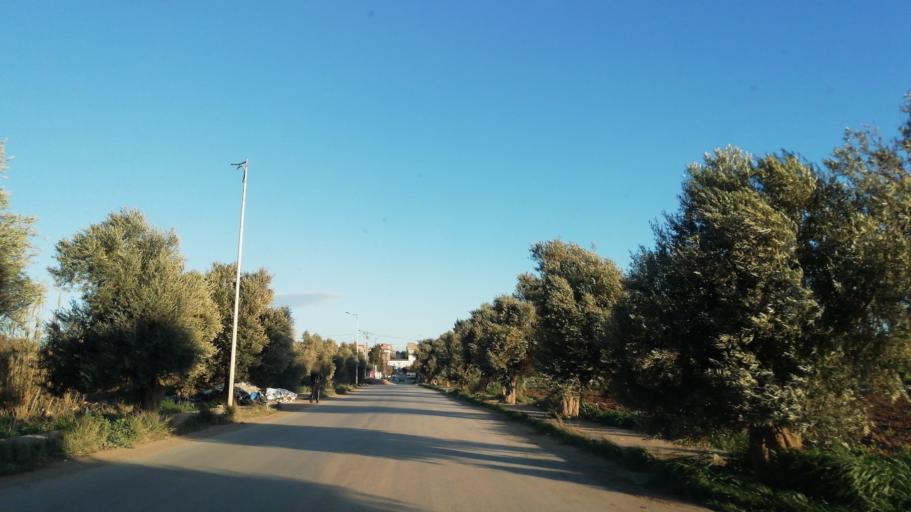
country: DZ
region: Oran
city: Sidi ech Chahmi
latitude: 35.6937
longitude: -0.5076
